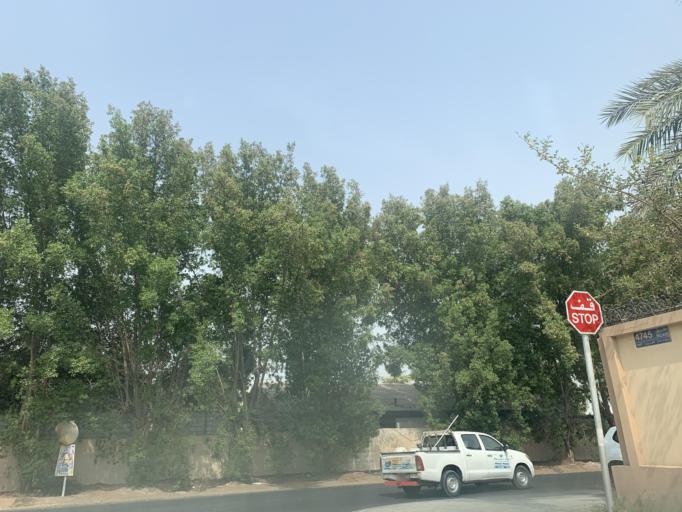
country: BH
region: Manama
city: Jidd Hafs
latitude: 26.2017
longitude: 50.4621
